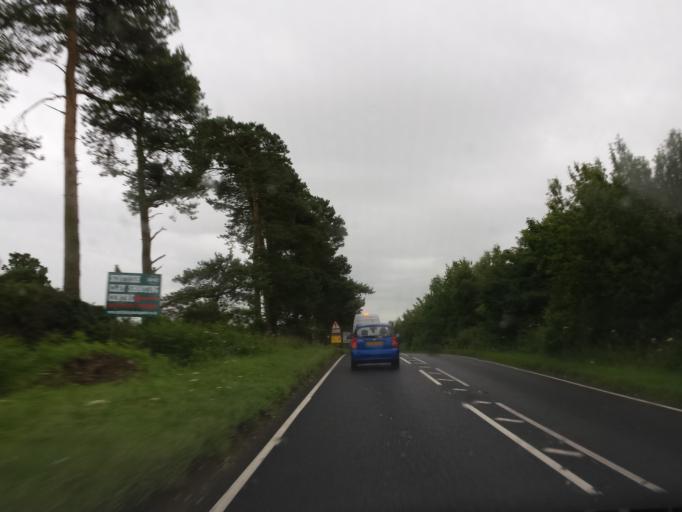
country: GB
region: Scotland
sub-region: Fife
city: Balmullo
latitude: 56.3966
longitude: -2.9086
